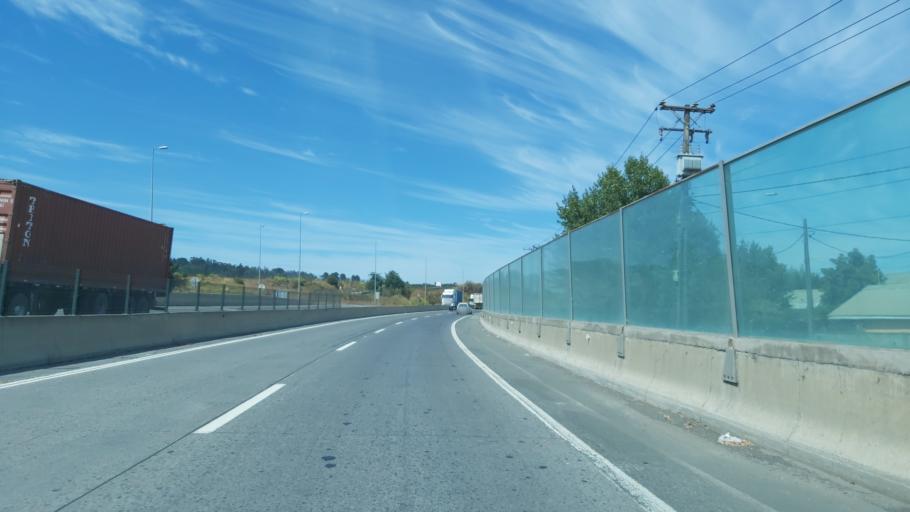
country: CL
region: Biobio
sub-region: Provincia de Concepcion
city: Coronel
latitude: -37.0396
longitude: -73.1353
